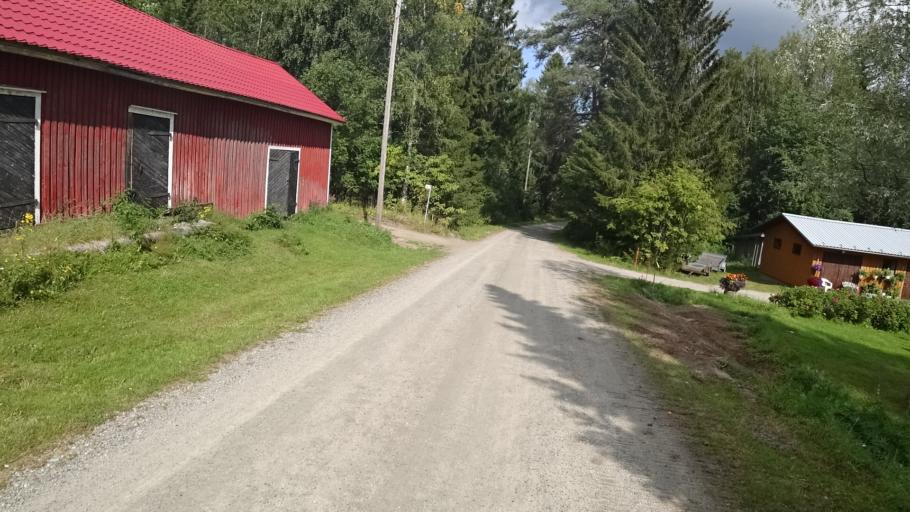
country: FI
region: North Karelia
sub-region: Joensuu
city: Ilomantsi
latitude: 62.6362
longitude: 31.2794
